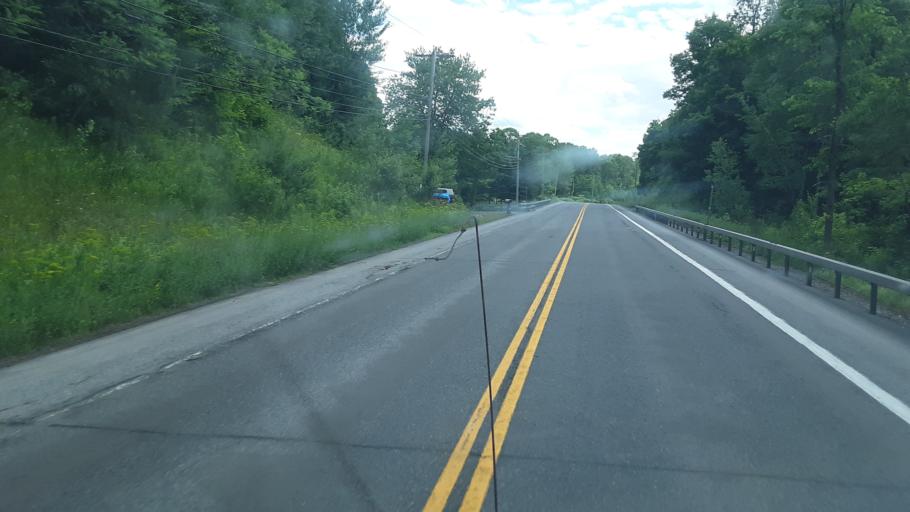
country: US
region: New York
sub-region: Oneida County
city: Rome
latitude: 43.3640
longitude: -75.4805
